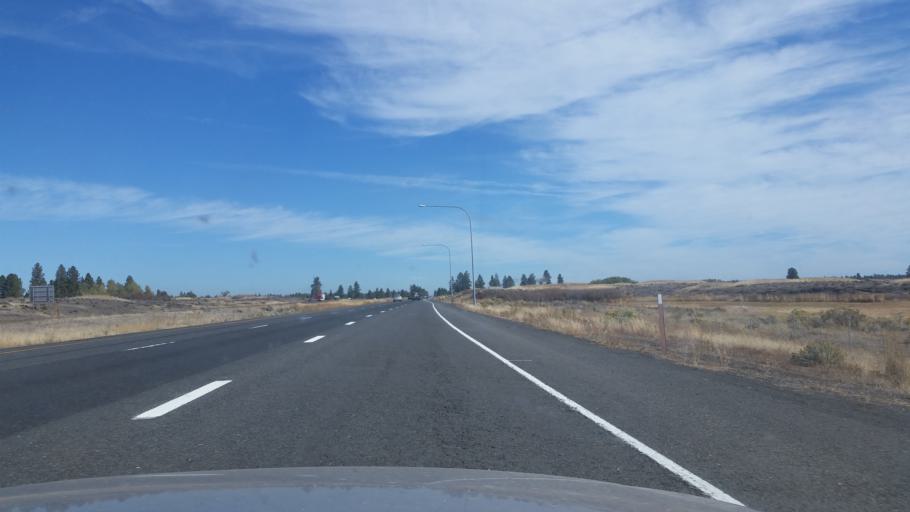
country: US
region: Washington
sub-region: Spokane County
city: Medical Lake
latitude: 47.3982
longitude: -117.8365
